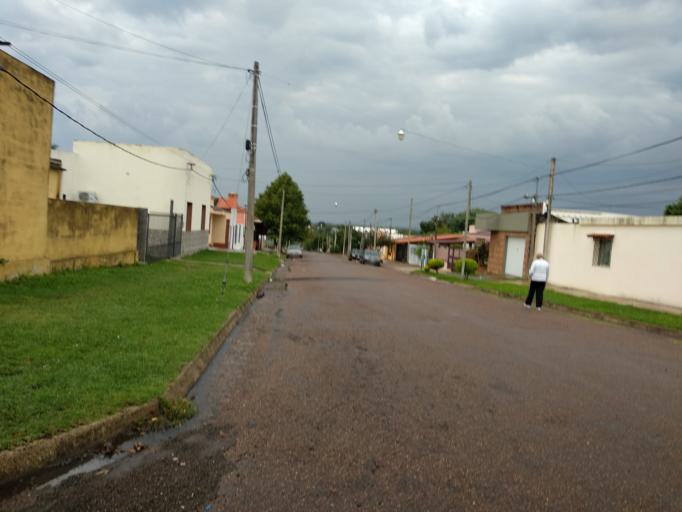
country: UY
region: Artigas
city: Artigas
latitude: -30.4072
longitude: -56.4692
